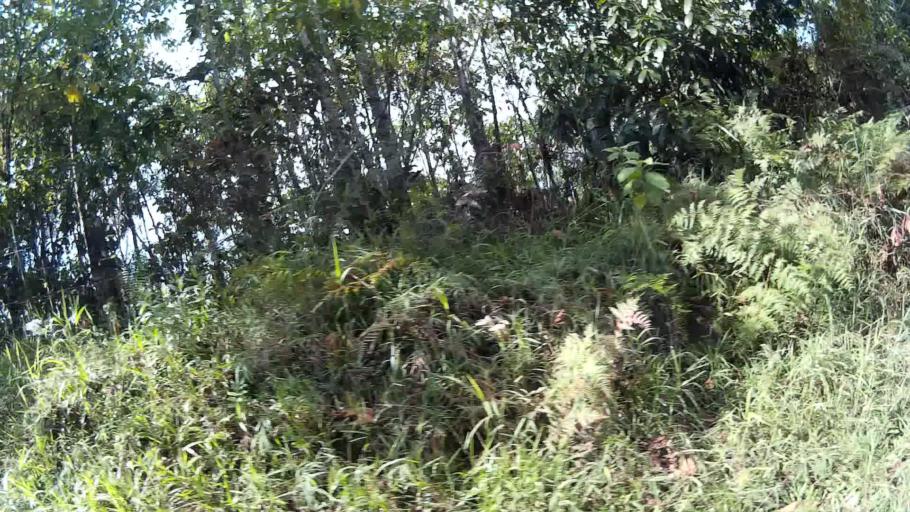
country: CO
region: Quindio
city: Filandia
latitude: 4.6879
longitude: -75.6254
